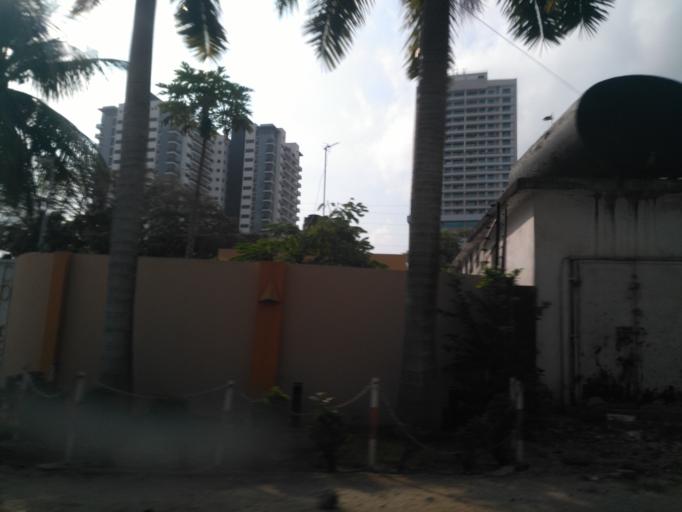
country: TZ
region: Dar es Salaam
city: Dar es Salaam
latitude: -6.8090
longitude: 39.2846
